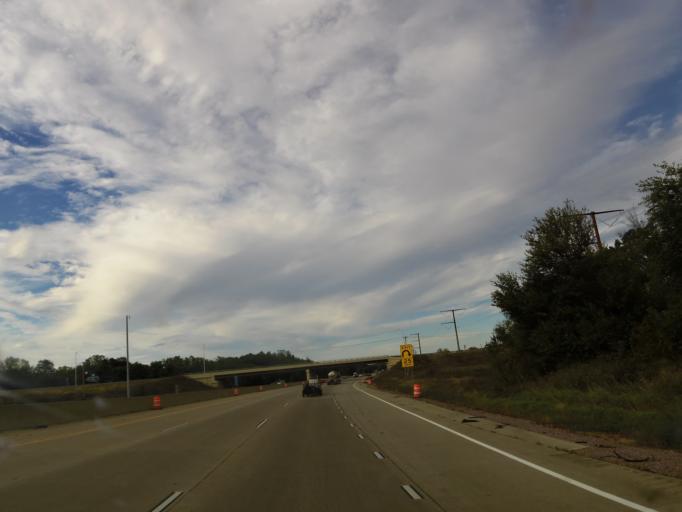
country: US
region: Wisconsin
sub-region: Columbia County
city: Poynette
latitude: 43.3900
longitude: -89.4665
